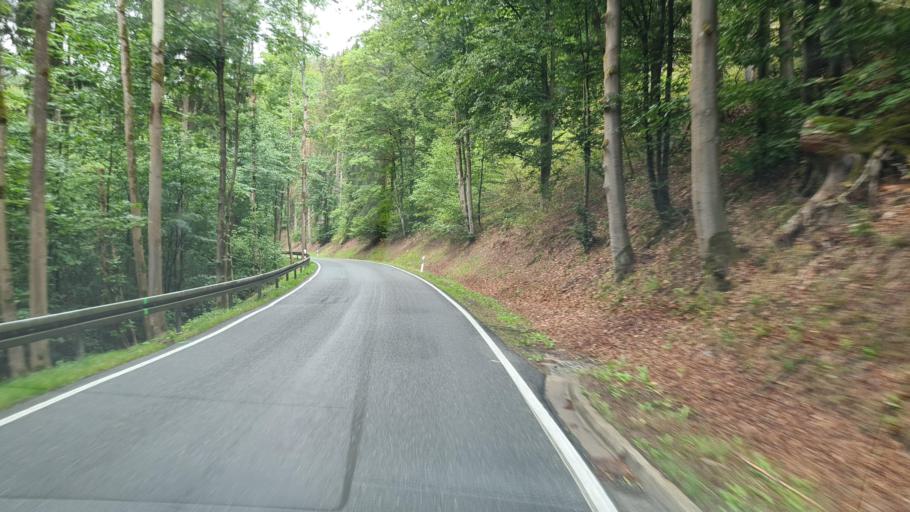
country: DE
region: Thuringia
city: Leutenberg
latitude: 50.5445
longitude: 11.4813
